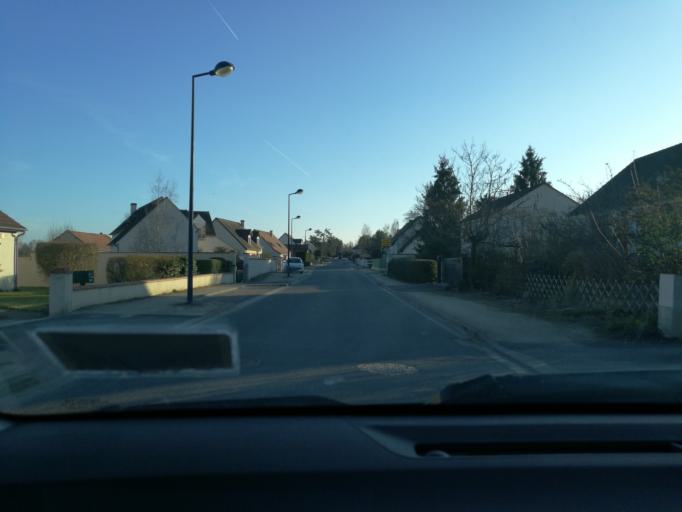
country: FR
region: Centre
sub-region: Departement du Loiret
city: Semoy
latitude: 47.9331
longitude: 1.9540
